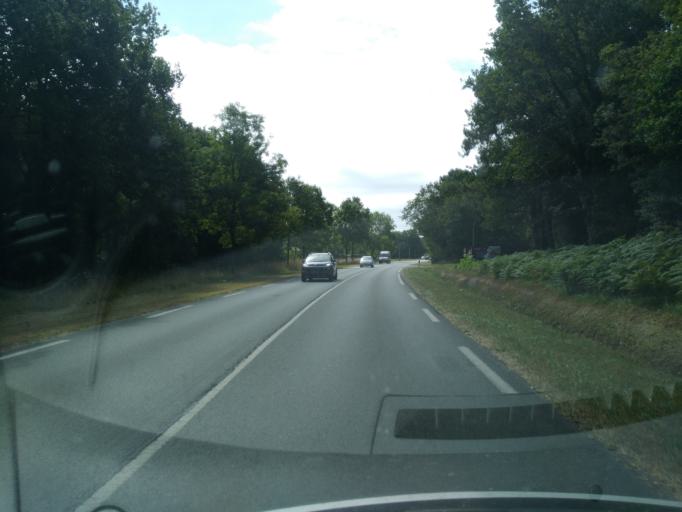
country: FR
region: Poitou-Charentes
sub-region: Departement de la Charente-Maritime
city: Chaillevette
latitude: 45.7157
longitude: -1.0687
